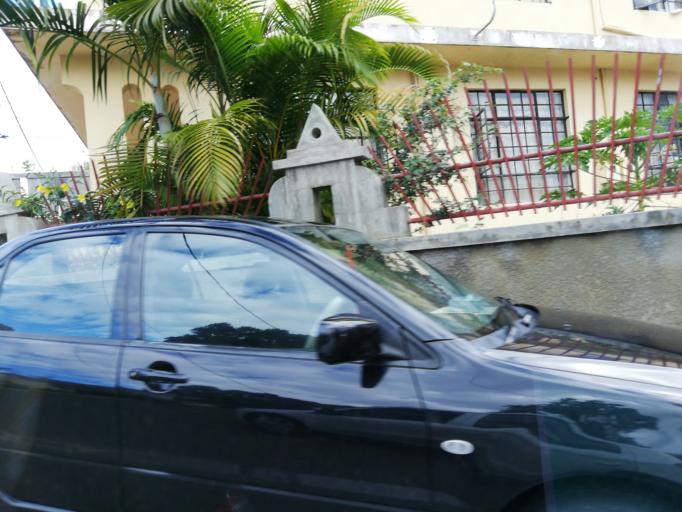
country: MU
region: Plaines Wilhems
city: Ebene
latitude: -20.2325
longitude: 57.4621
